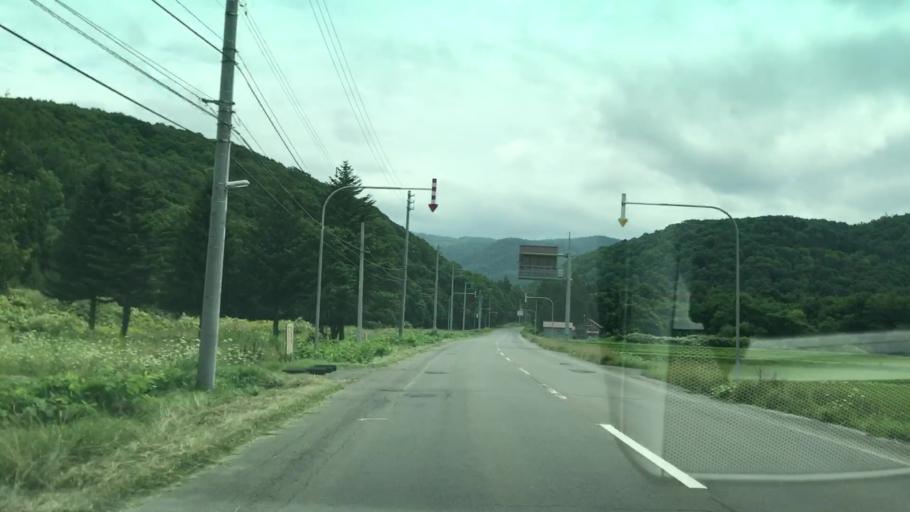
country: JP
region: Hokkaido
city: Yoichi
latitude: 43.0486
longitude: 140.8469
